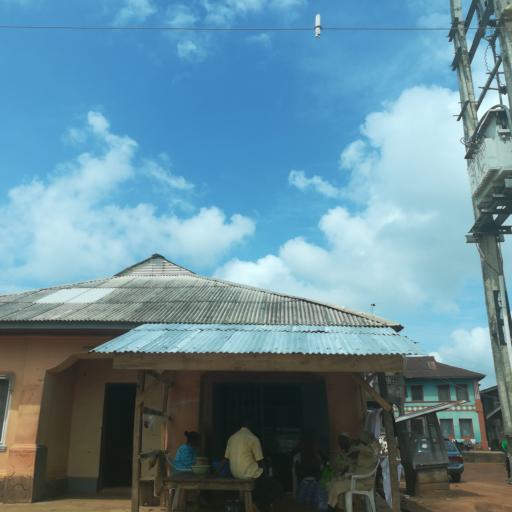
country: NG
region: Lagos
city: Ejirin
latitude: 6.6451
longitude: 3.7134
